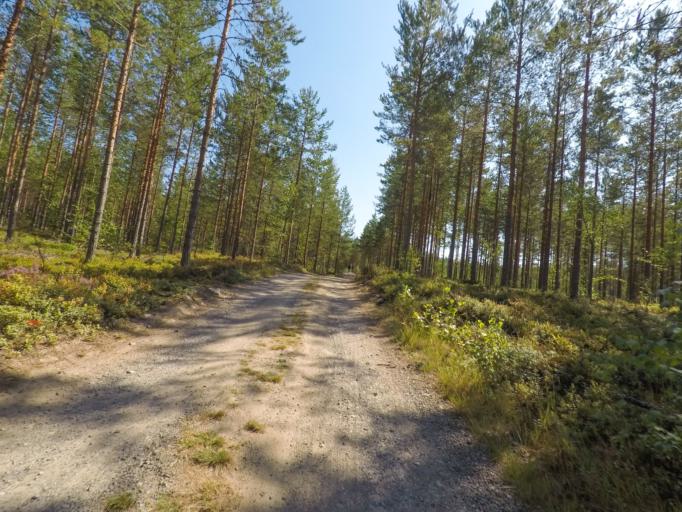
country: FI
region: Southern Savonia
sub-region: Mikkeli
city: Puumala
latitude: 61.4281
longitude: 28.0070
